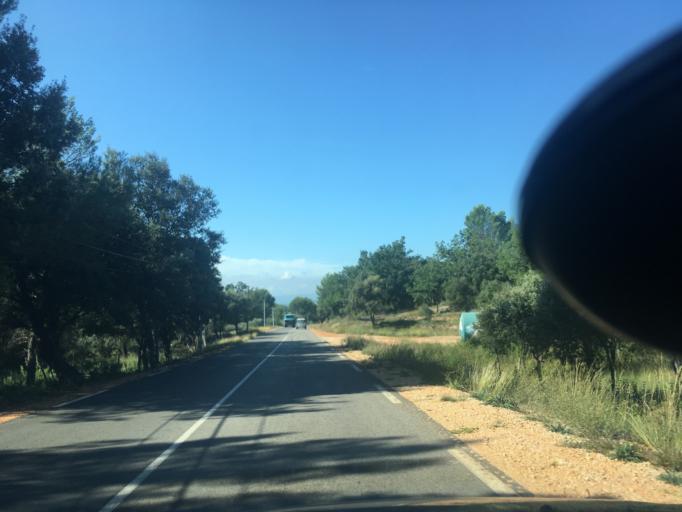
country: FR
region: Provence-Alpes-Cote d'Azur
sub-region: Departement du Var
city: Barjols
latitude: 43.6009
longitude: 6.0453
